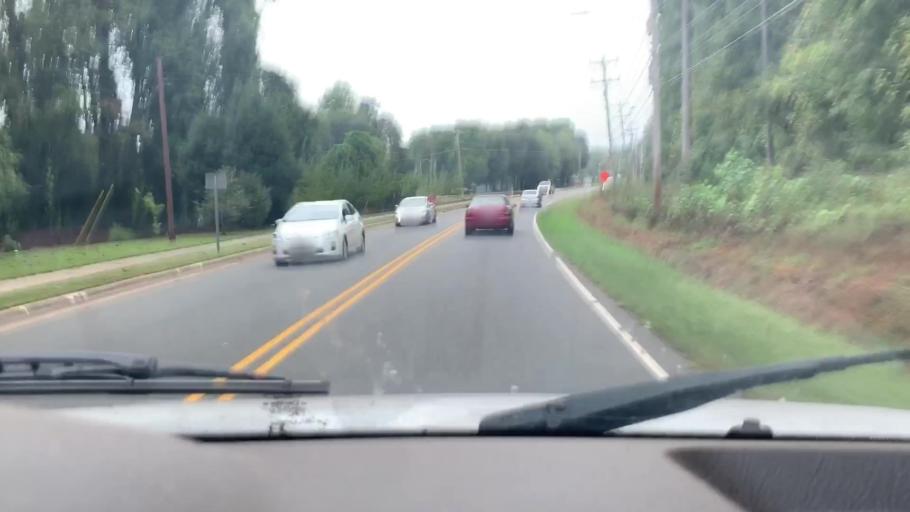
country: US
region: North Carolina
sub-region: Gaston County
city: Davidson
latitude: 35.5074
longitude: -80.8431
